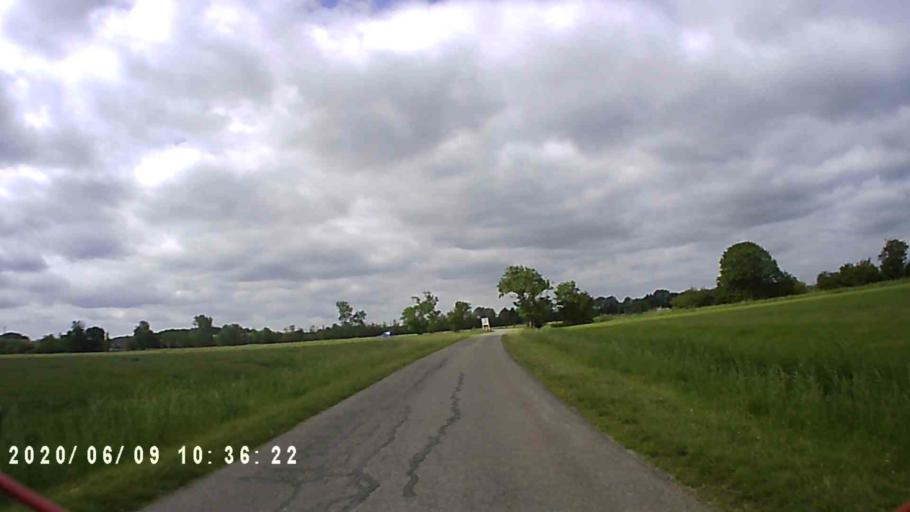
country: NL
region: Groningen
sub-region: Gemeente Groningen
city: Korrewegwijk
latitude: 53.2569
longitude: 6.5252
